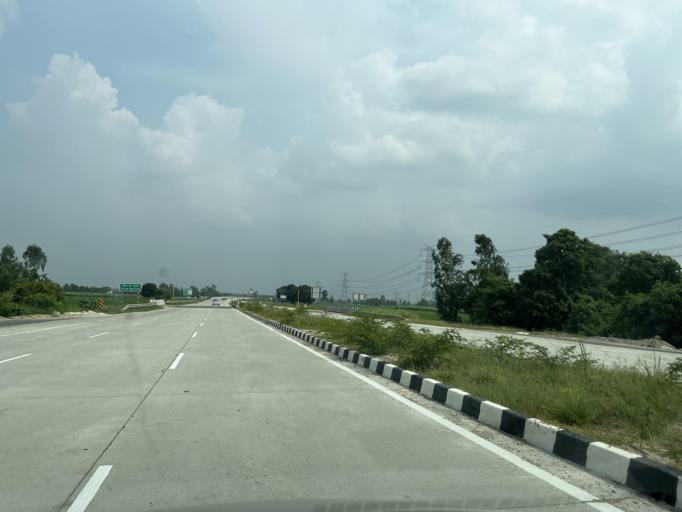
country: IN
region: Uttarakhand
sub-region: Udham Singh Nagar
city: Jaspur
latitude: 29.2928
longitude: 78.8466
